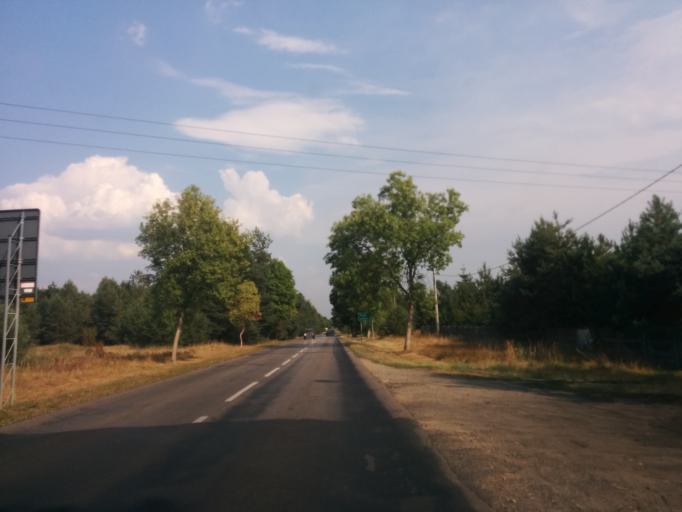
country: PL
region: Silesian Voivodeship
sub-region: Powiat myszkowski
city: Zarki-Letnisko
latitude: 50.6044
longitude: 19.2762
